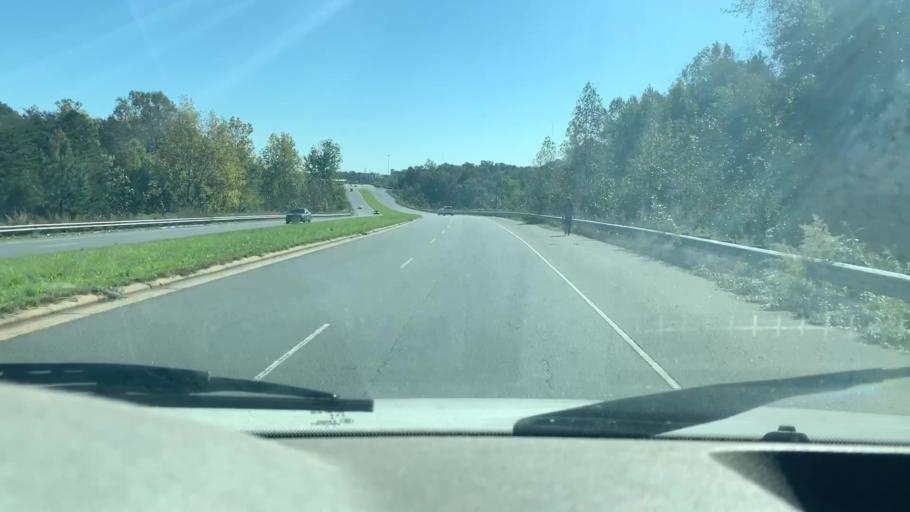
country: US
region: North Carolina
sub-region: Mecklenburg County
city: Charlotte
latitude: 35.2940
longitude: -80.7776
